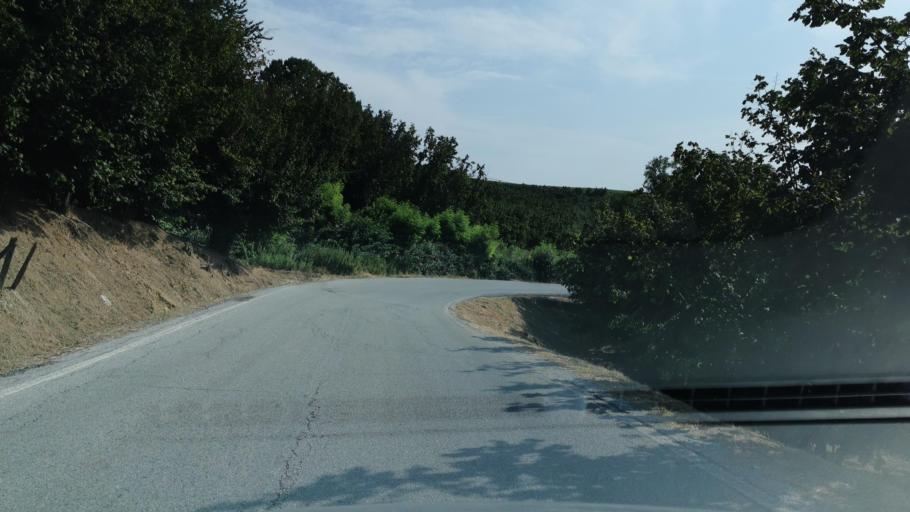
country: IT
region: Piedmont
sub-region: Provincia di Cuneo
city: La Morra
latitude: 44.6450
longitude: 7.9143
